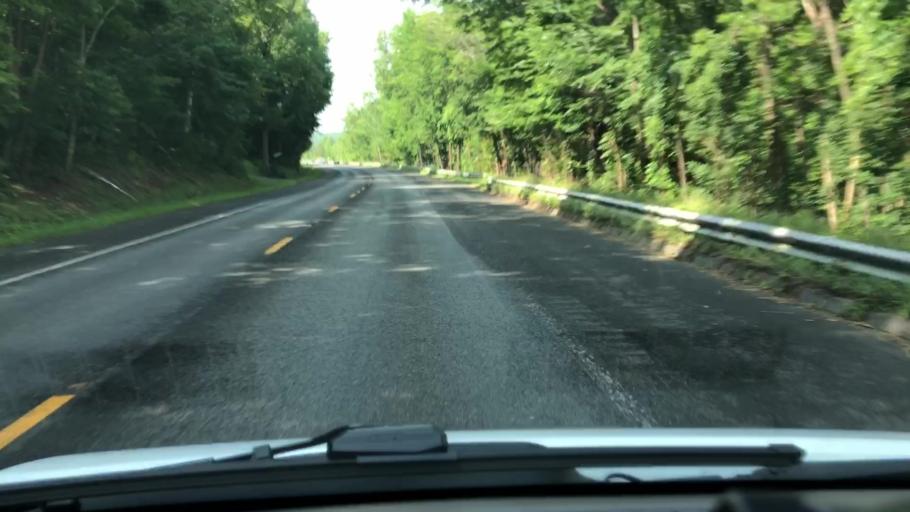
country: US
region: Massachusetts
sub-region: Berkshire County
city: Lanesborough
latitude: 42.5337
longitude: -73.1861
